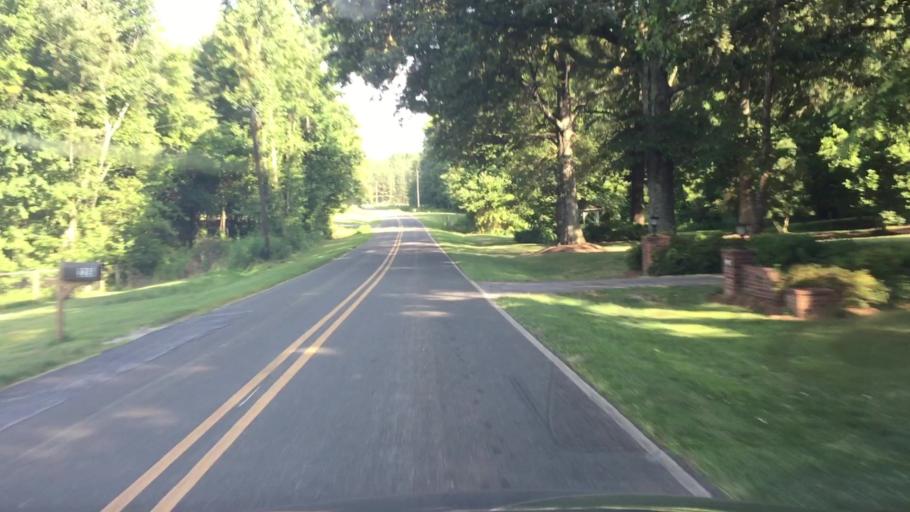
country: US
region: North Carolina
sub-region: Rockingham County
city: Reidsville
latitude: 36.2808
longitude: -79.5940
